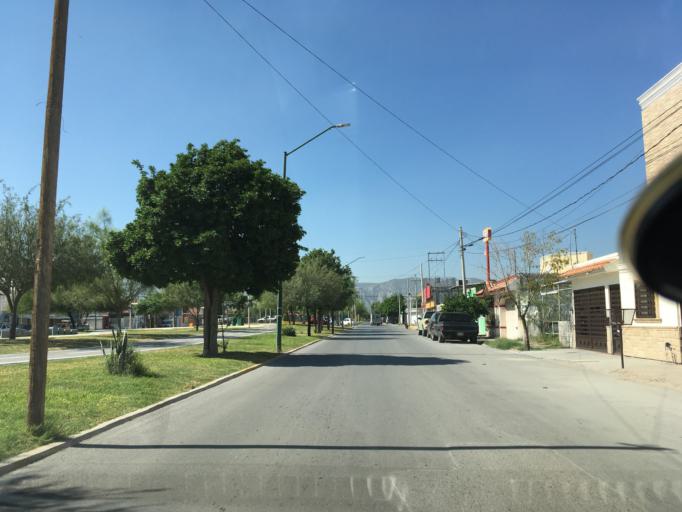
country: MX
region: Coahuila
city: Torreon
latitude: 25.5180
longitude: -103.3828
